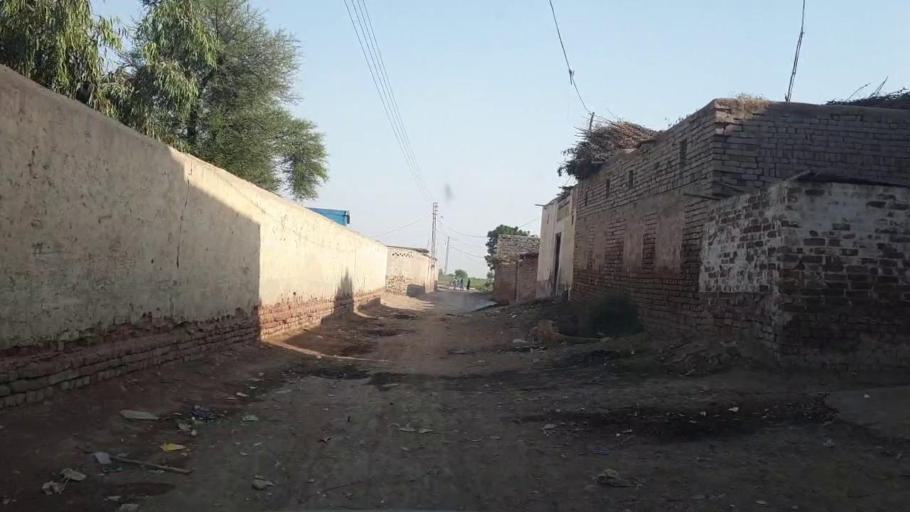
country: PK
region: Sindh
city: Sanghar
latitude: 26.0570
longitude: 68.8843
